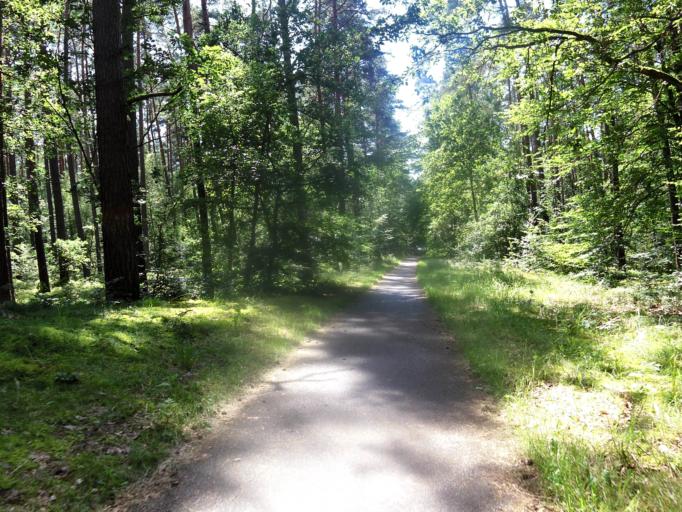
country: DE
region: Brandenburg
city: Lychen
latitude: 53.1914
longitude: 13.2384
